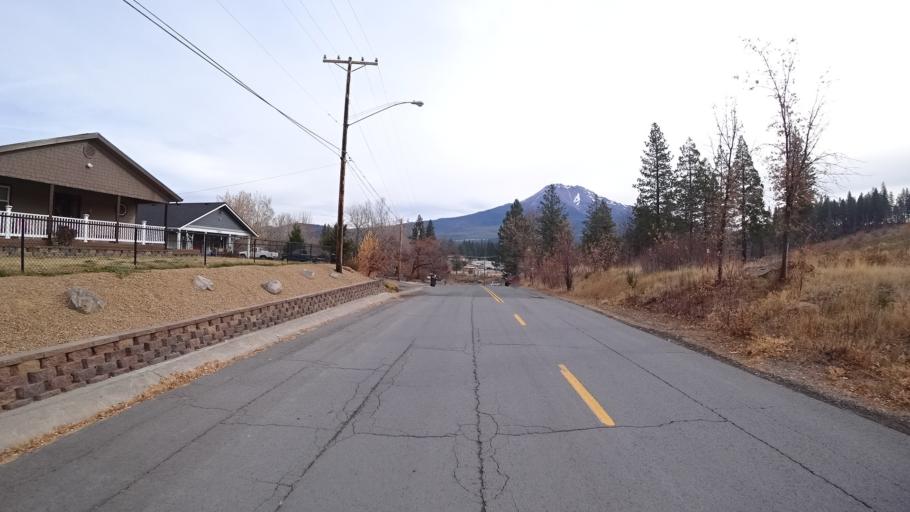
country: US
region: California
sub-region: Siskiyou County
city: Weed
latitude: 41.4273
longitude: -122.3772
